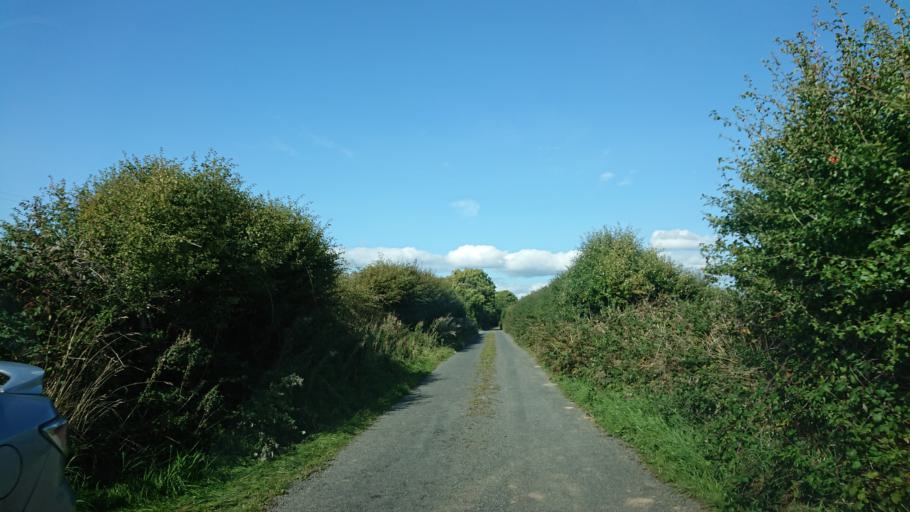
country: IE
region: Munster
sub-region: Waterford
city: Waterford
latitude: 52.2082
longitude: -7.0561
